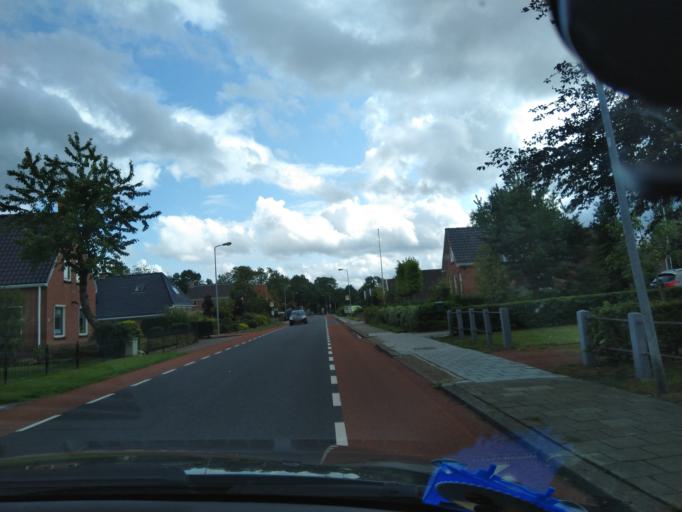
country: NL
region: Groningen
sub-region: Gemeente Zuidhorn
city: Aduard
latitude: 53.2280
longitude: 6.5001
